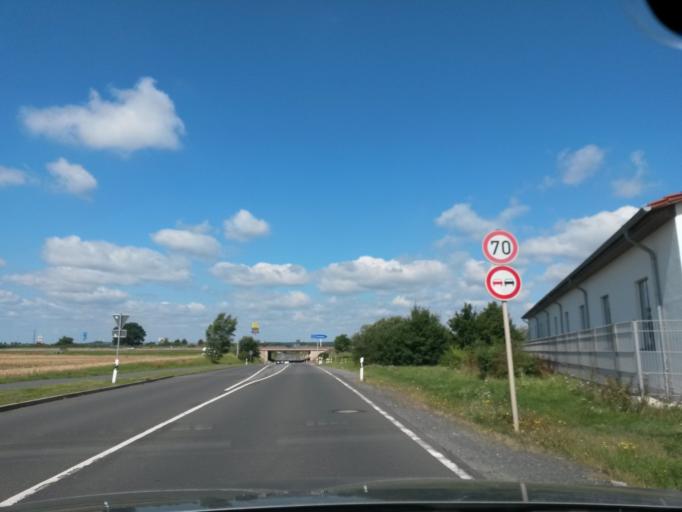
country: DE
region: Thuringia
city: Reichenbach
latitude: 50.8886
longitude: 11.8787
